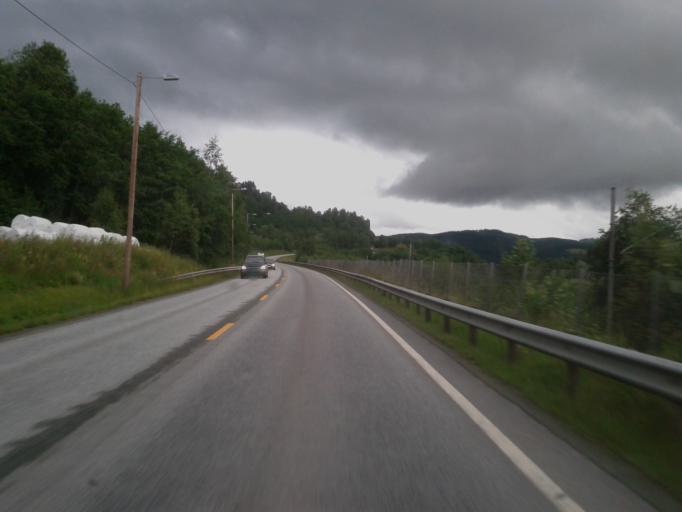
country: NO
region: Sor-Trondelag
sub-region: Melhus
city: Lundamo
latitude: 63.1189
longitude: 10.2438
